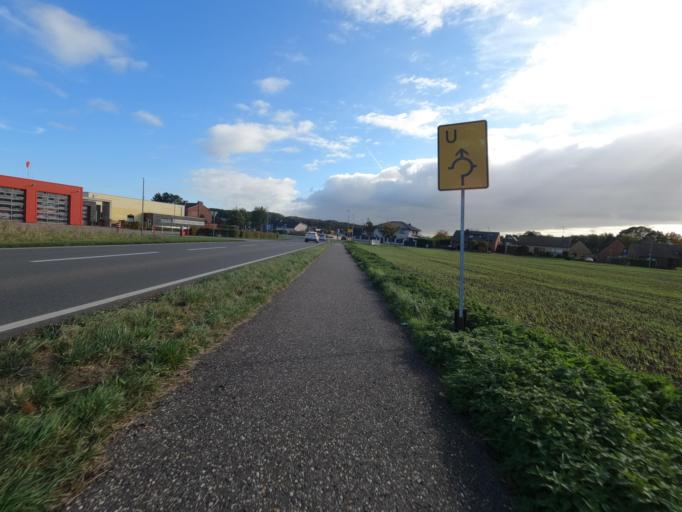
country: DE
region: North Rhine-Westphalia
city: Huckelhoven
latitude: 51.0465
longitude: 6.2400
